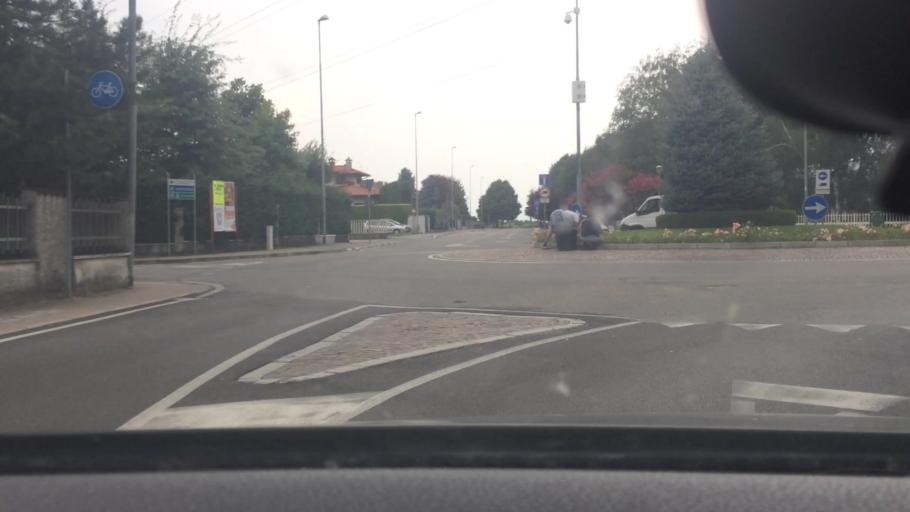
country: IT
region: Lombardy
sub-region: Provincia di Monza e Brianza
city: Ceriano Laghetto
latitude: 45.6312
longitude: 9.0761
